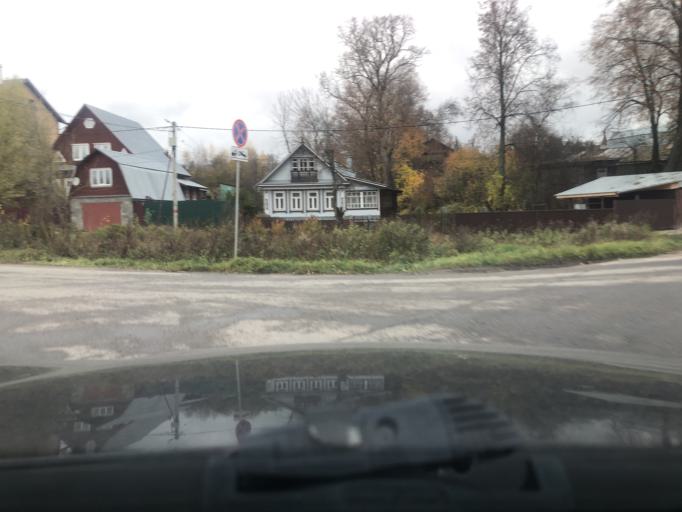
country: RU
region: Moskovskaya
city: Sergiyev Posad
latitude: 56.3040
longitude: 38.1243
